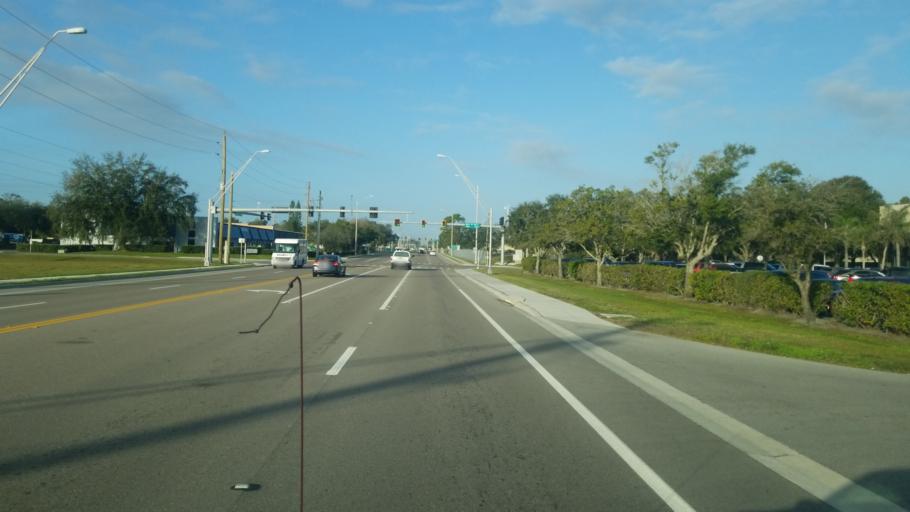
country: US
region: Florida
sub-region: Manatee County
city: Samoset
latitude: 27.4622
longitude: -82.5390
